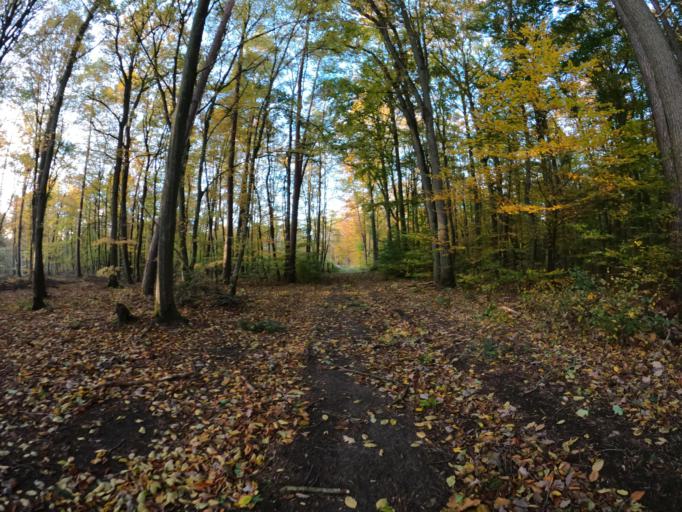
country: PL
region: West Pomeranian Voivodeship
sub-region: Powiat mysliborski
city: Barlinek
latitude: 52.9521
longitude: 15.2429
